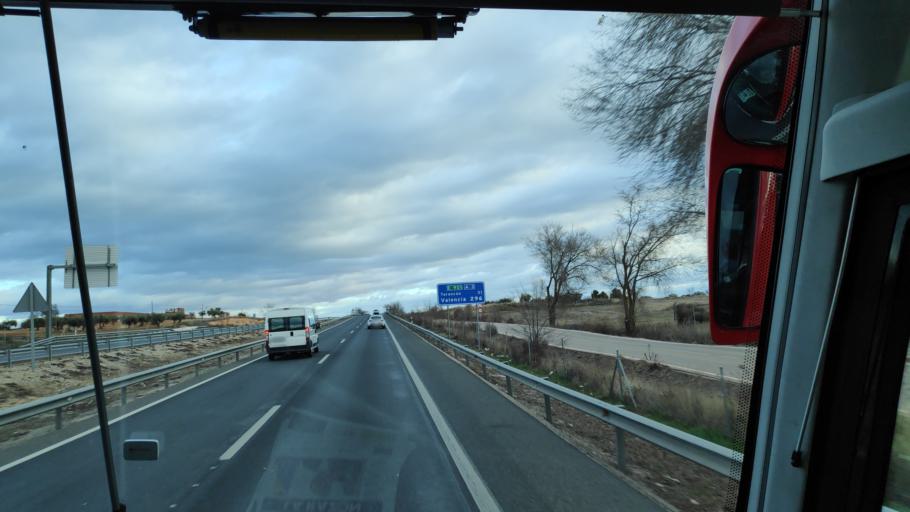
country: ES
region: Madrid
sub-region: Provincia de Madrid
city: Villarejo de Salvanes
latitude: 40.1600
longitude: -3.2626
